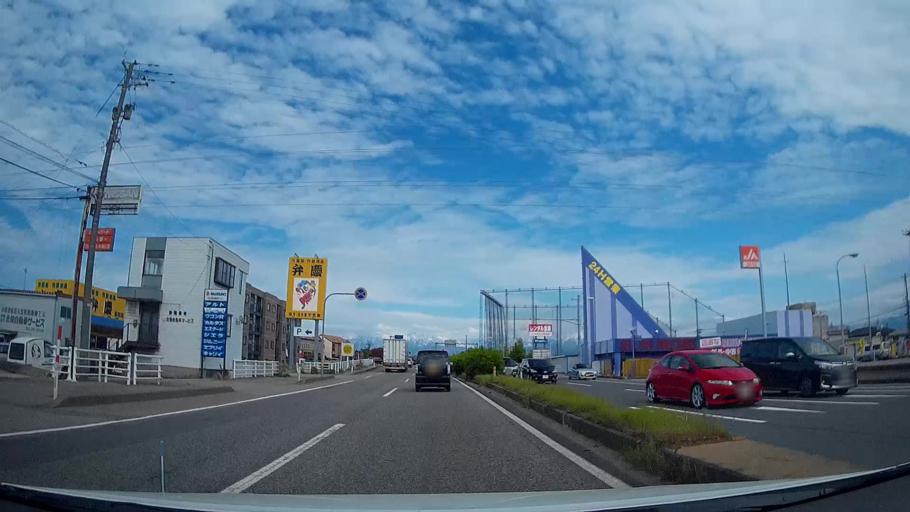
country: JP
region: Toyama
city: Toyama-shi
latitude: 36.7242
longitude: 137.2373
